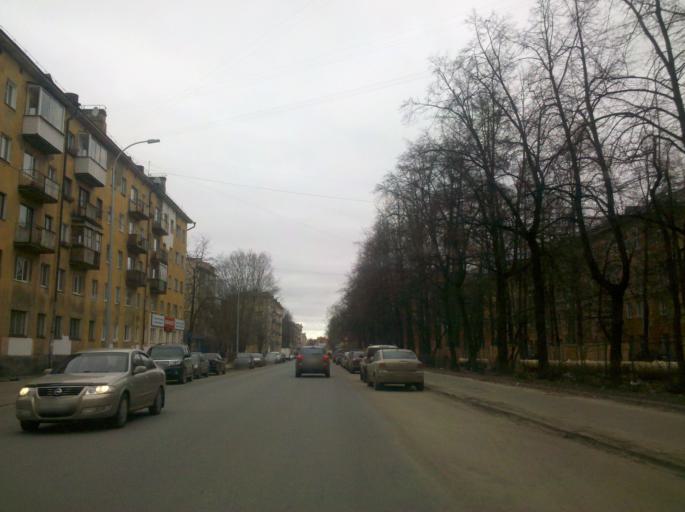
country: RU
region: Republic of Karelia
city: Petrozavodsk
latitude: 61.7824
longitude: 34.3558
